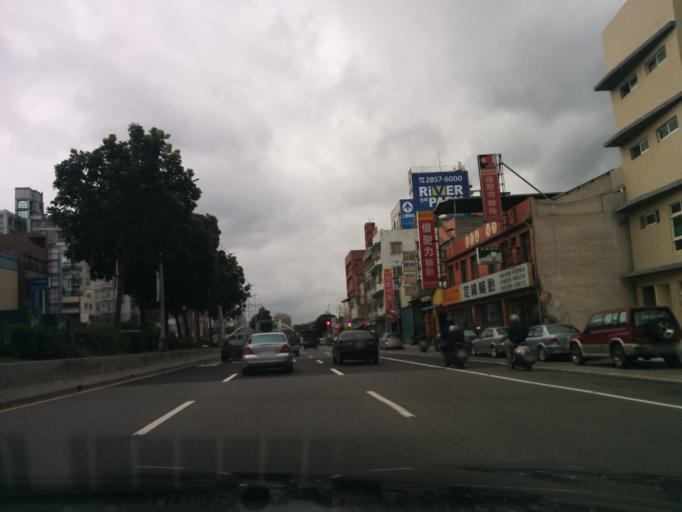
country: TW
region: Taipei
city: Taipei
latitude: 25.0923
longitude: 121.4993
